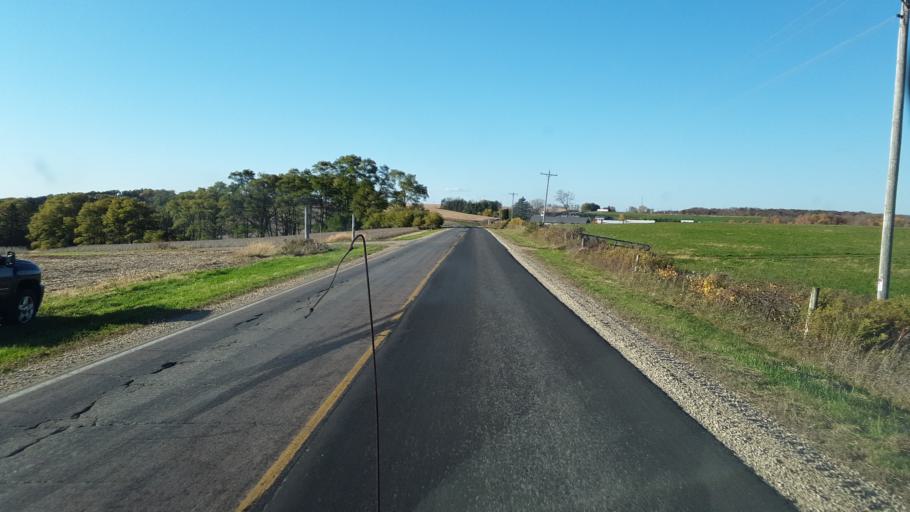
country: US
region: Wisconsin
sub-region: Vernon County
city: Hillsboro
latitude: 43.6507
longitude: -90.4541
